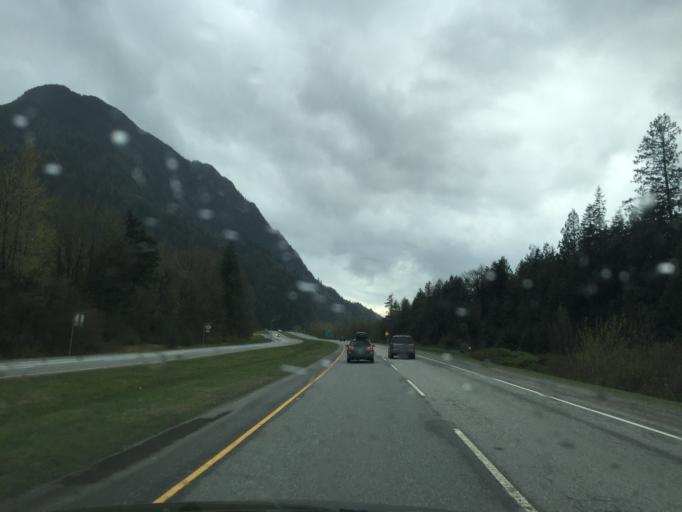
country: CA
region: British Columbia
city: Agassiz
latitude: 49.3167
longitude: -121.6296
